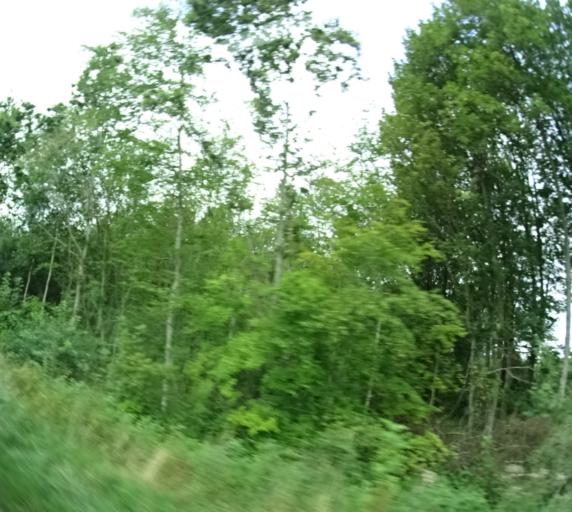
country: DK
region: Central Jutland
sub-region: Syddjurs Kommune
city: Ryomgard
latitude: 56.3955
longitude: 10.5155
